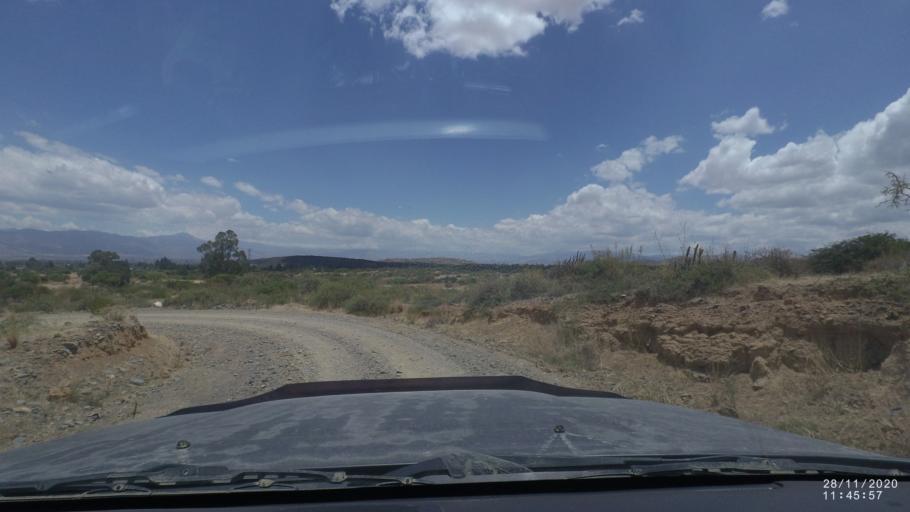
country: BO
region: Cochabamba
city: Tarata
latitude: -17.6535
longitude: -66.0427
